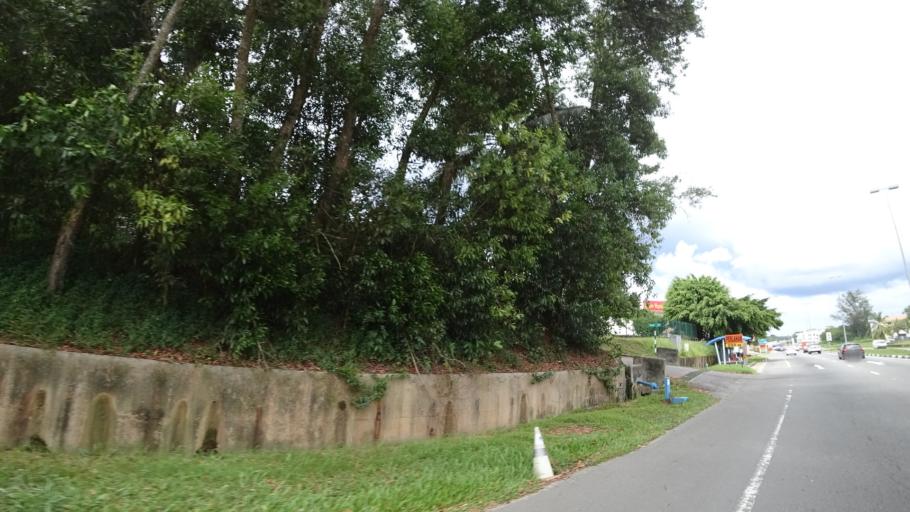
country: BN
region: Brunei and Muara
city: Bandar Seri Begawan
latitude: 4.8800
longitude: 114.8863
